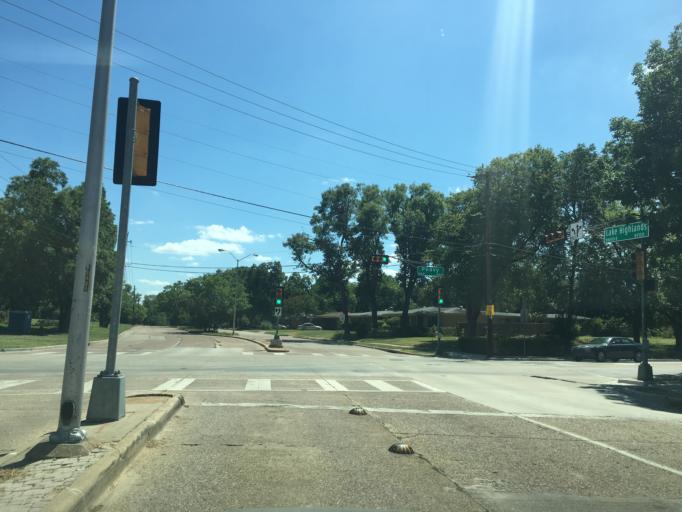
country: US
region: Texas
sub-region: Dallas County
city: Highland Park
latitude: 32.8450
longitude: -96.7051
